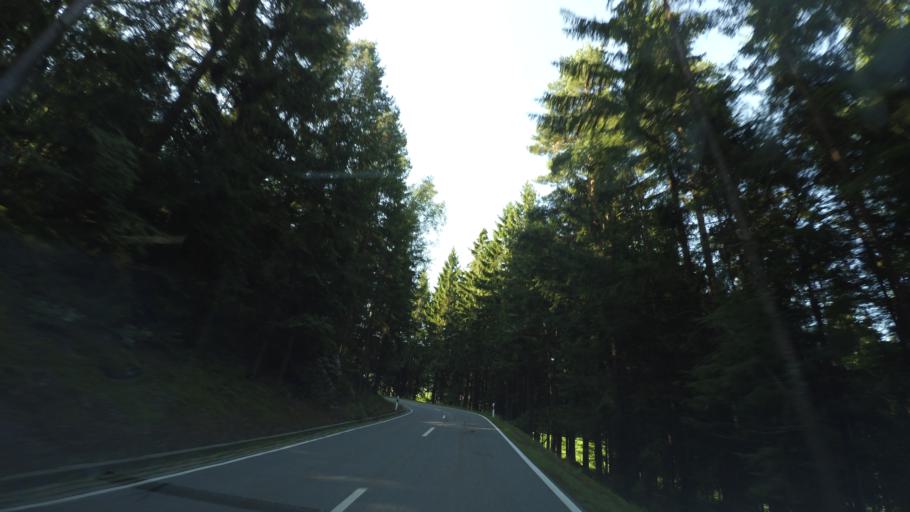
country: DE
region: Bavaria
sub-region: Upper Palatinate
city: Arrach
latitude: 49.1820
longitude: 13.0074
